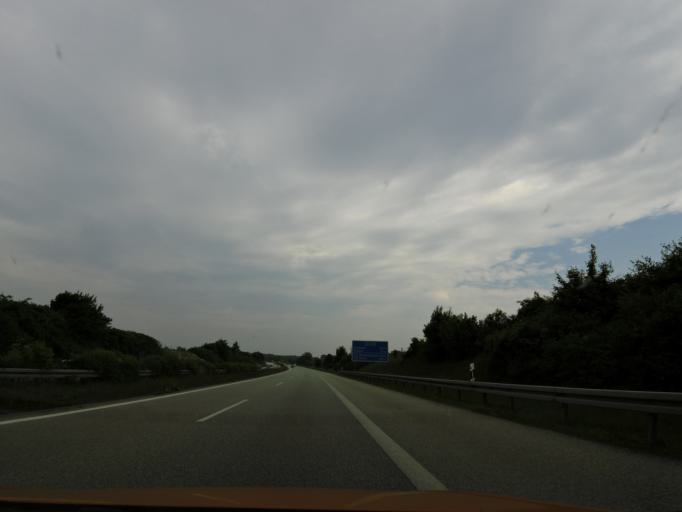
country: DE
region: Mecklenburg-Vorpommern
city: Bobitz
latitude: 53.8227
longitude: 11.3483
